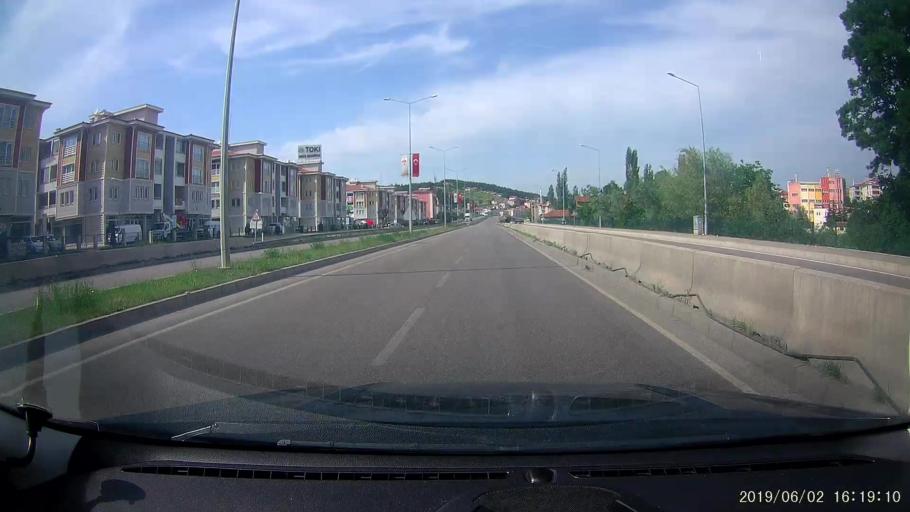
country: TR
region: Samsun
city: Havza
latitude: 40.9641
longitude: 35.6674
